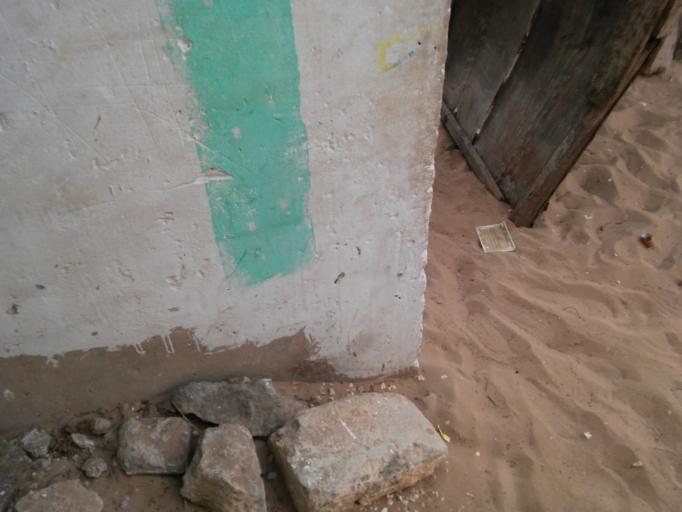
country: SN
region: Dakar
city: Pikine
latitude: 14.7421
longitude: -17.4190
